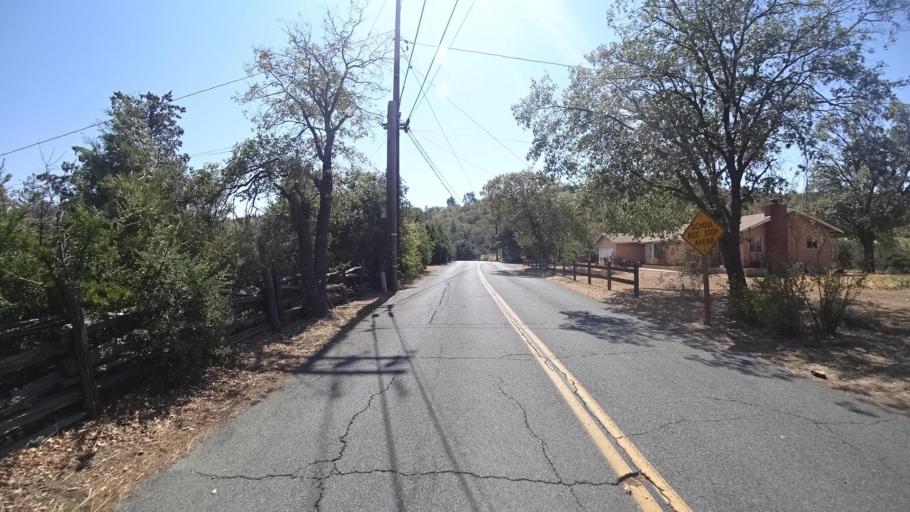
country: US
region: California
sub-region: San Diego County
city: Julian
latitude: 33.0762
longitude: -116.5883
